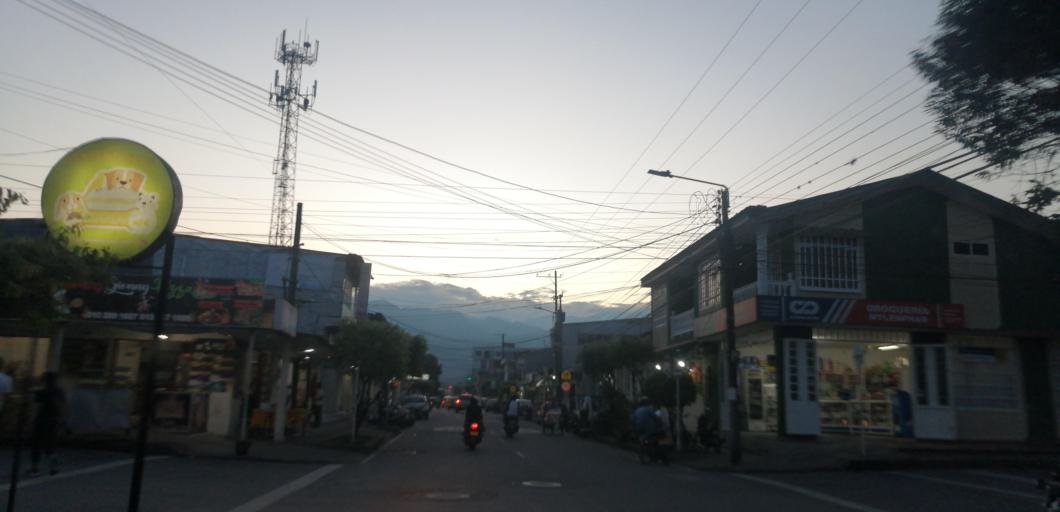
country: CO
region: Meta
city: Acacias
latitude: 3.9875
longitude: -73.7686
